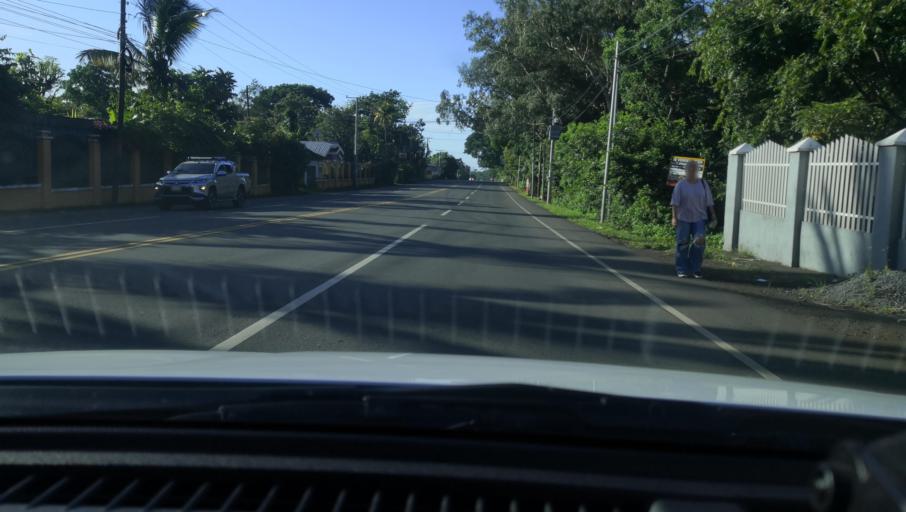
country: NI
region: Carazo
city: Jinotepe
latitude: 11.8346
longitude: -86.1808
